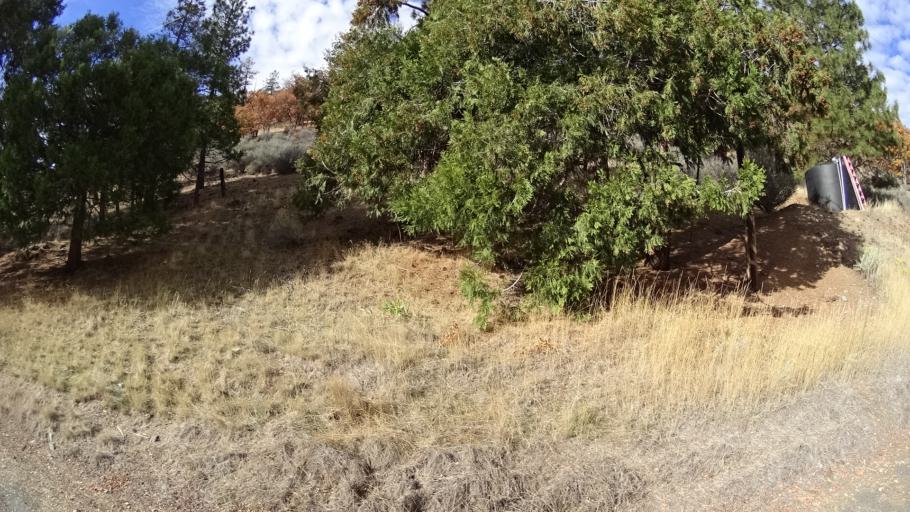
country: US
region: California
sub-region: Siskiyou County
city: Yreka
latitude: 41.6395
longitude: -122.7513
